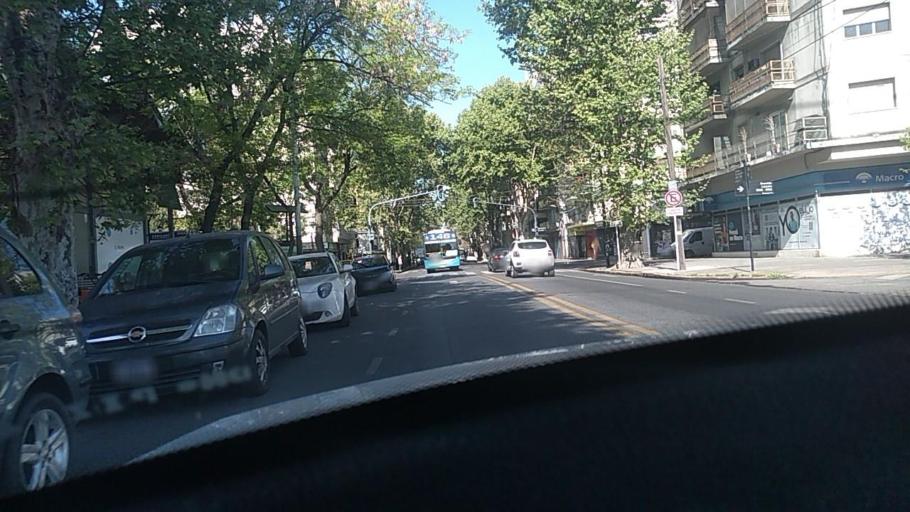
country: AR
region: Buenos Aires F.D.
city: Villa Santa Rita
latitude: -34.6004
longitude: -58.5032
